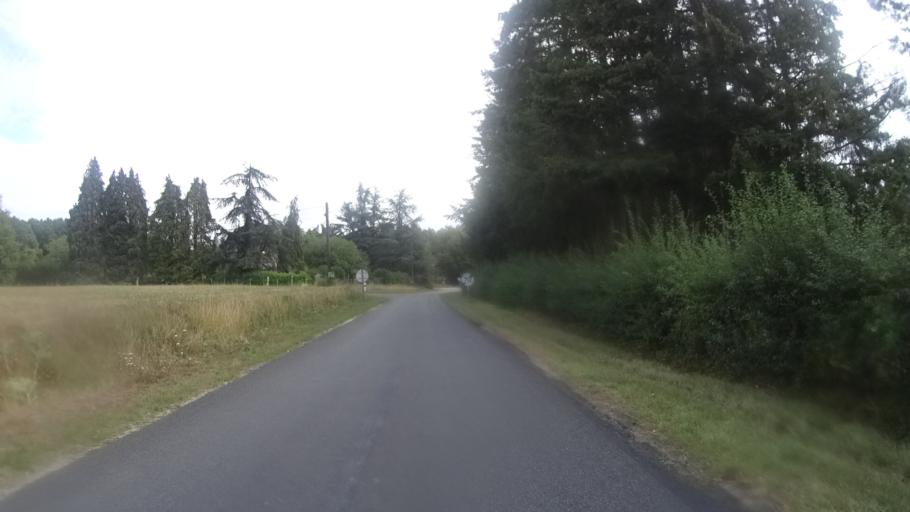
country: FR
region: Centre
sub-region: Departement du Loiret
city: Vitry-aux-Loges
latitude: 47.9971
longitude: 2.2241
